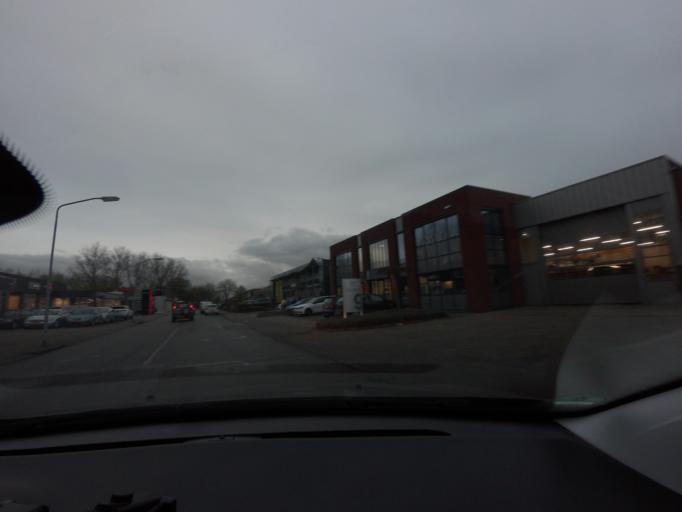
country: NL
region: Utrecht
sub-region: Gemeente Woerden
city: Woerden
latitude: 52.0795
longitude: 4.8792
